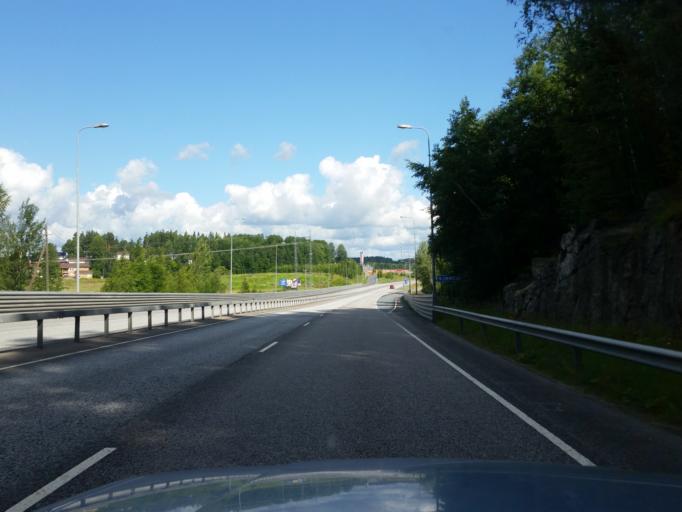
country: FI
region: Uusimaa
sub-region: Helsinki
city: Vihti
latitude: 60.3259
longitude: 24.3367
